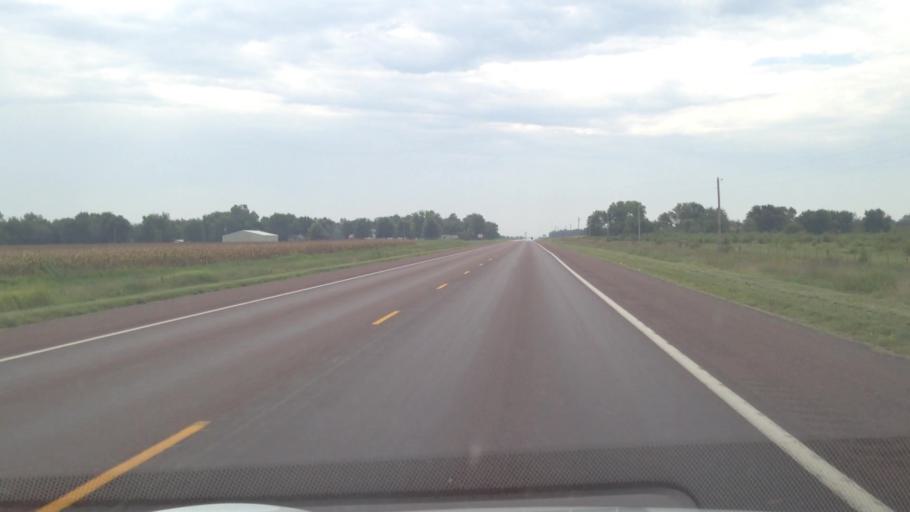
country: US
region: Kansas
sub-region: Crawford County
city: Girard
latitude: 37.4445
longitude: -94.8331
